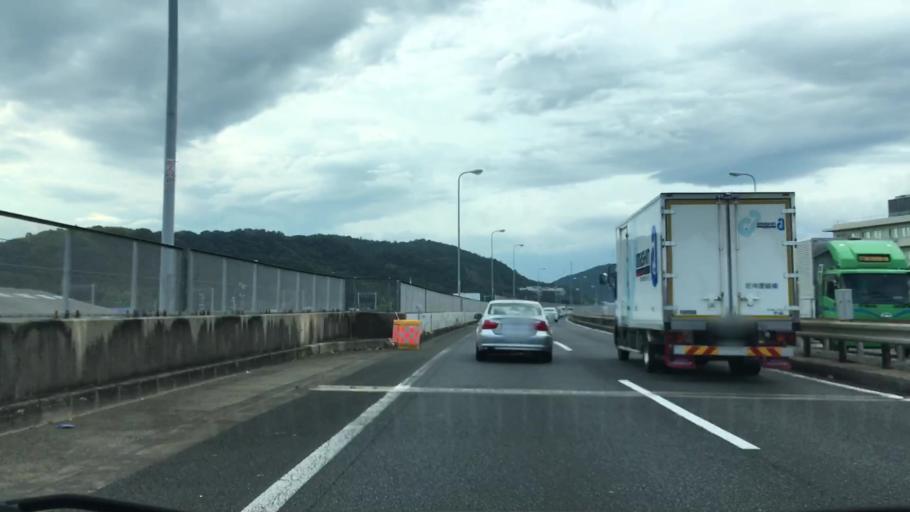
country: JP
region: Hyogo
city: Shirahamacho-usazakiminami
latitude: 34.7882
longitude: 134.7727
